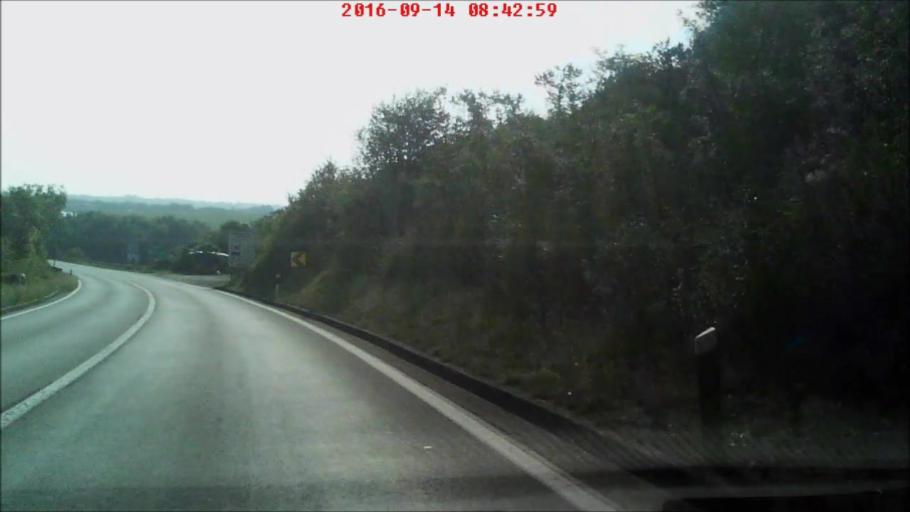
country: HR
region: Zadarska
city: Policnik
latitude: 44.1909
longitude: 15.4121
